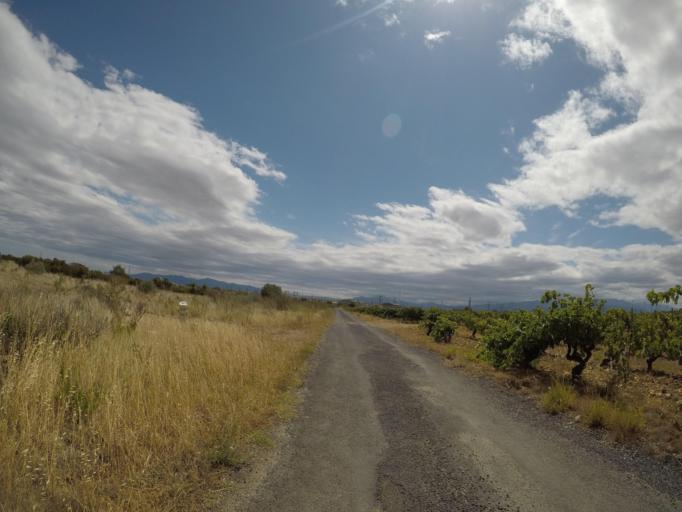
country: FR
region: Languedoc-Roussillon
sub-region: Departement des Pyrenees-Orientales
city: Baixas
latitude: 42.7391
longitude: 2.8030
